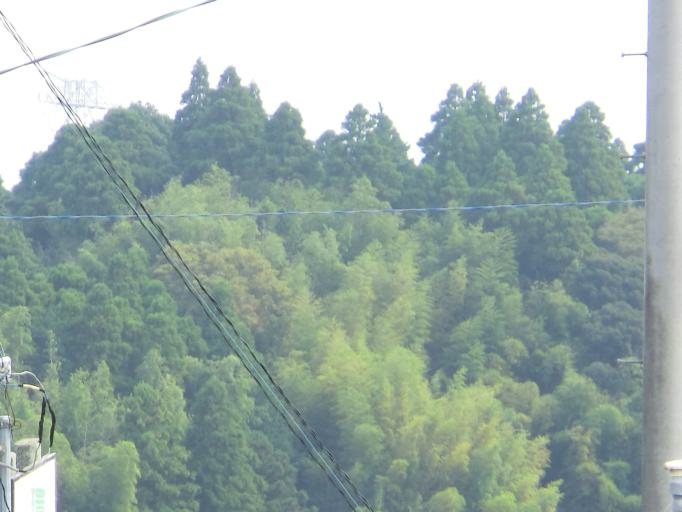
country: JP
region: Chiba
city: Yachimata
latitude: 35.6286
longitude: 140.3624
